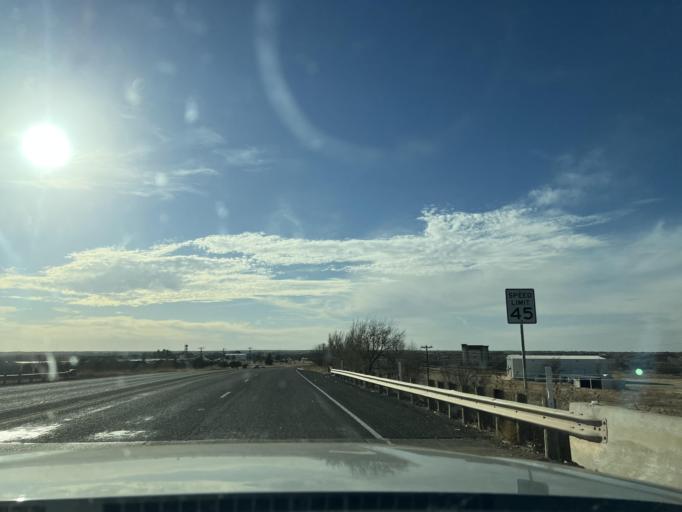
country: US
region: Texas
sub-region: Scurry County
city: Snyder
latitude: 32.7033
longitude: -100.8741
